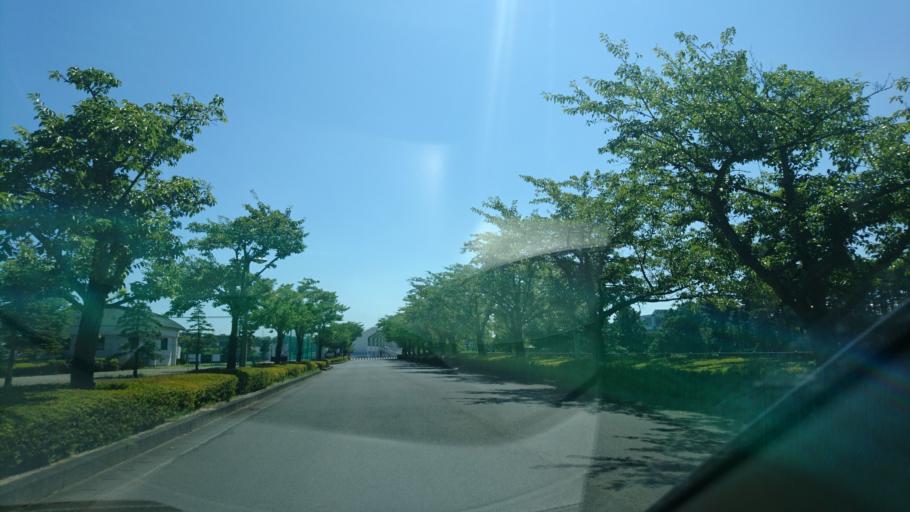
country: JP
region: Iwate
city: Kitakami
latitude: 39.2610
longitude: 141.0950
